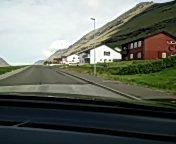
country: FO
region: Nordoyar
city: Klaksvik
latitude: 62.2993
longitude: -6.5213
